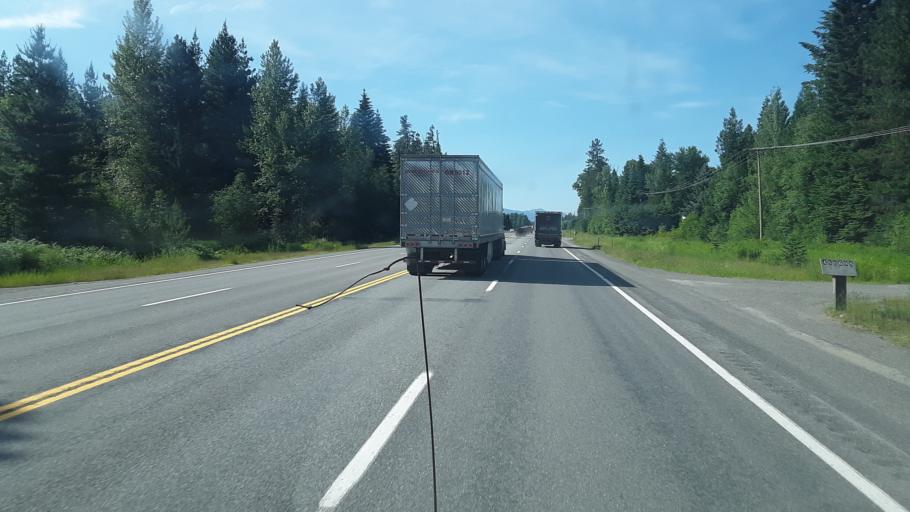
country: US
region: Idaho
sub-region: Bonner County
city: Ponderay
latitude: 48.3616
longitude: -116.5476
